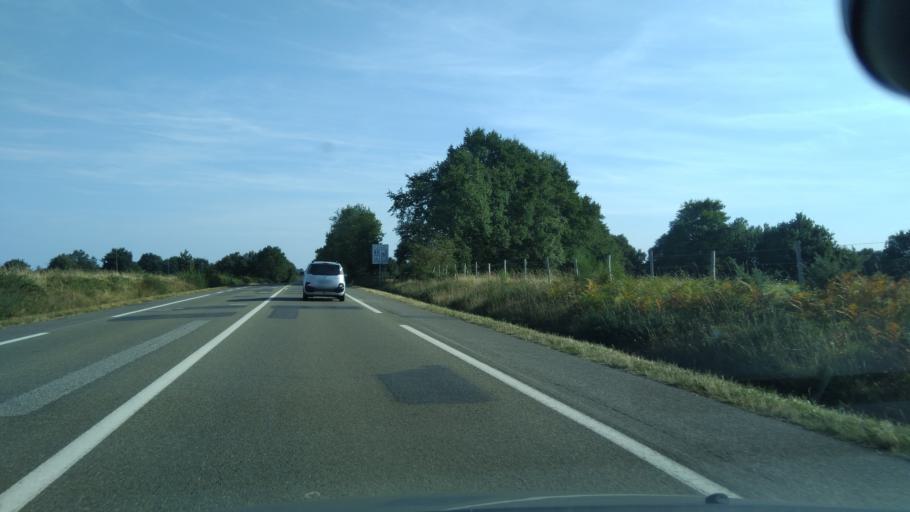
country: FR
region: Pays de la Loire
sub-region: Departement de la Mayenne
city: Entrammes
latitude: 47.9868
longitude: -0.7123
